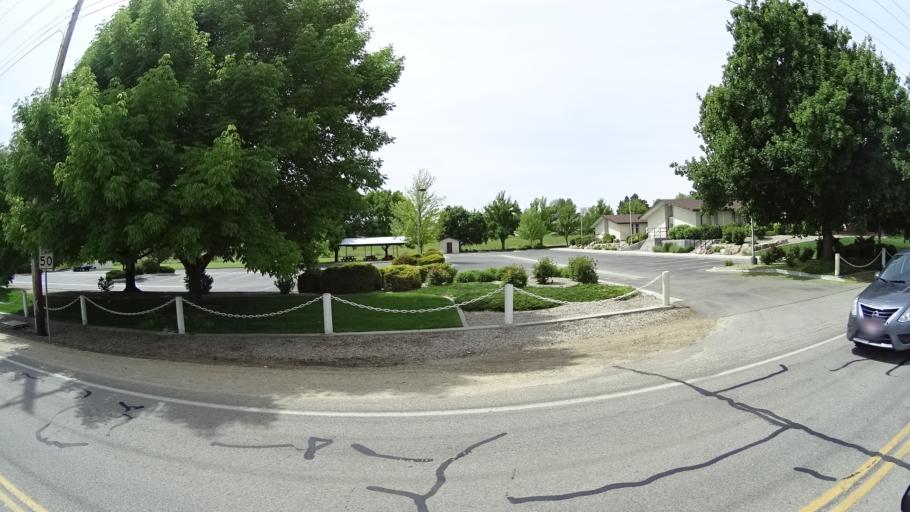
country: US
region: Idaho
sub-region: Ada County
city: Meridian
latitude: 43.5612
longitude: -116.3729
